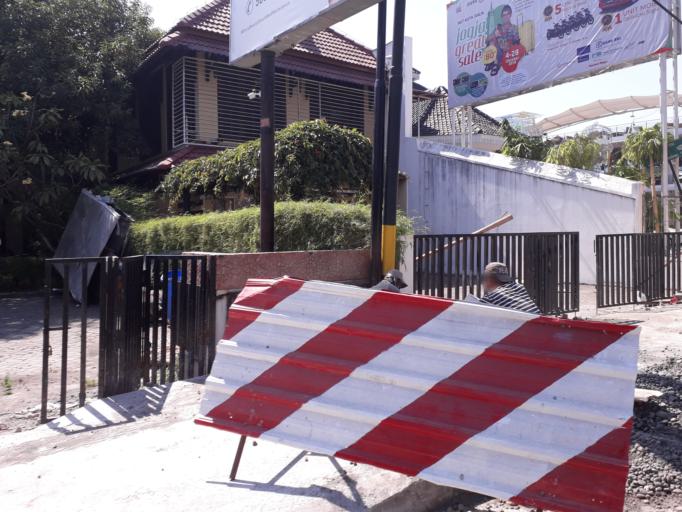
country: ID
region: Daerah Istimewa Yogyakarta
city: Yogyakarta
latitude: -7.7849
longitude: 110.3747
